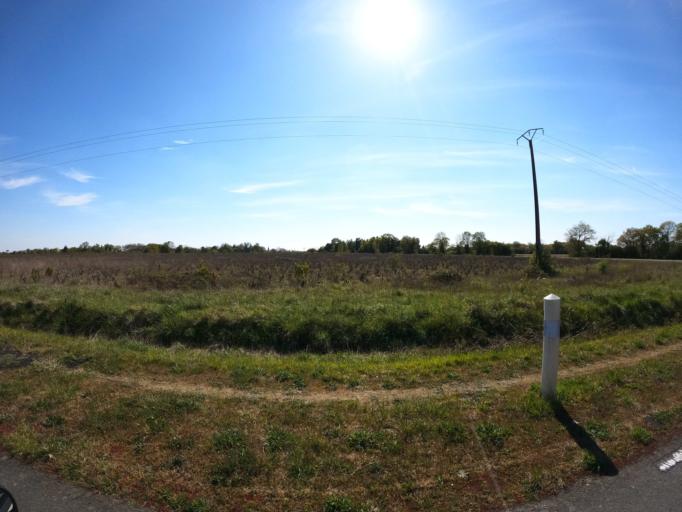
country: FR
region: Pays de la Loire
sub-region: Departement de la Loire-Atlantique
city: Gorges
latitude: 47.1134
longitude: -1.2929
